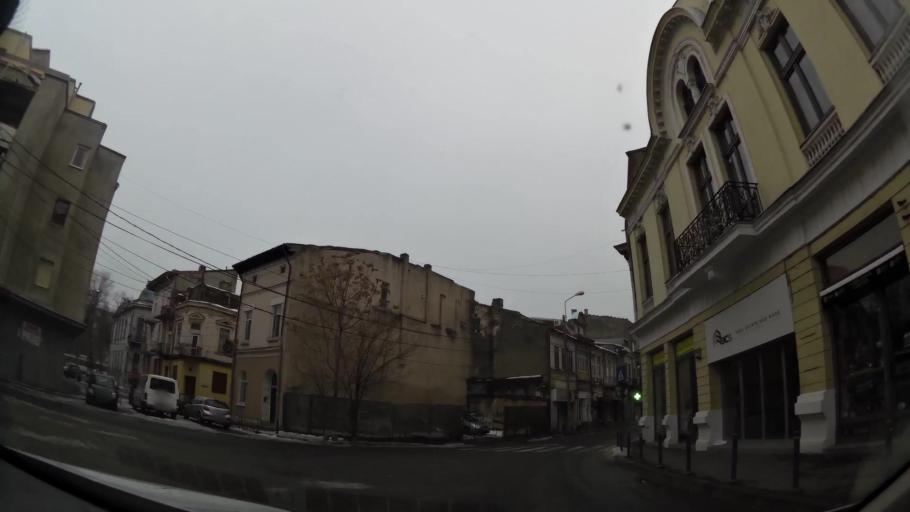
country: RO
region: Bucuresti
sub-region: Municipiul Bucuresti
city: Bucharest
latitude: 44.4339
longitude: 26.1051
